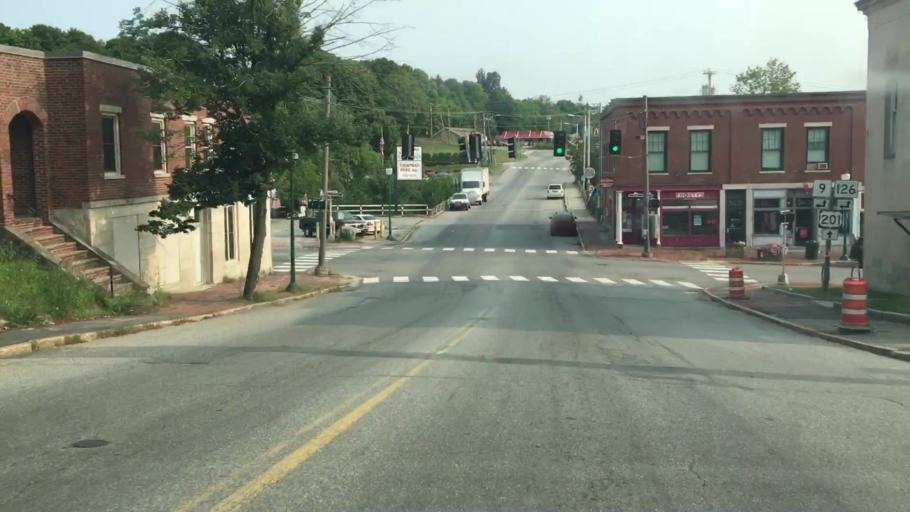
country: US
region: Maine
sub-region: Kennebec County
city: Gardiner
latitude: 44.2296
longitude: -69.7747
